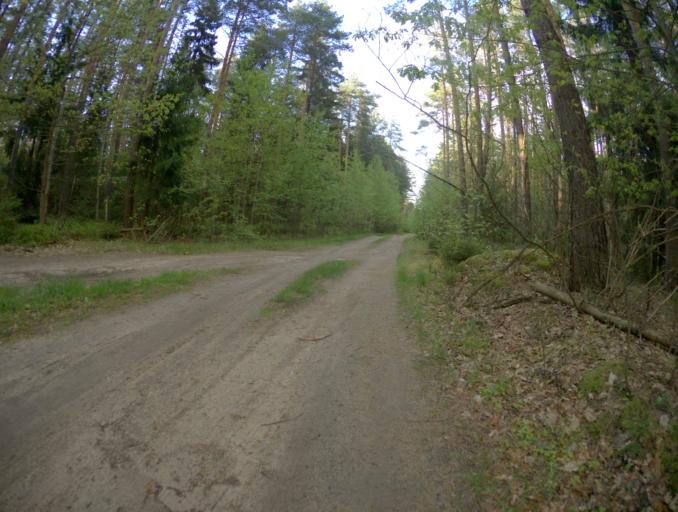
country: RU
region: Rjazan
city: Spas-Klepiki
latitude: 55.2494
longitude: 40.0897
